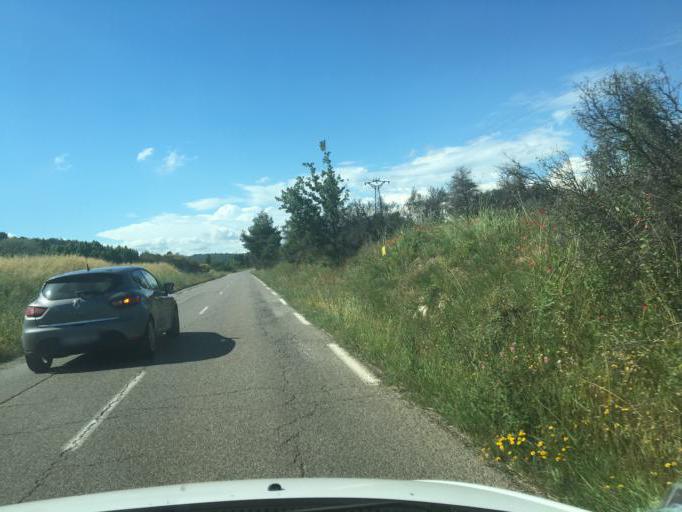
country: FR
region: Provence-Alpes-Cote d'Azur
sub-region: Departement des Bouches-du-Rhone
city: Eguilles
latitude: 43.5321
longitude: 5.3503
